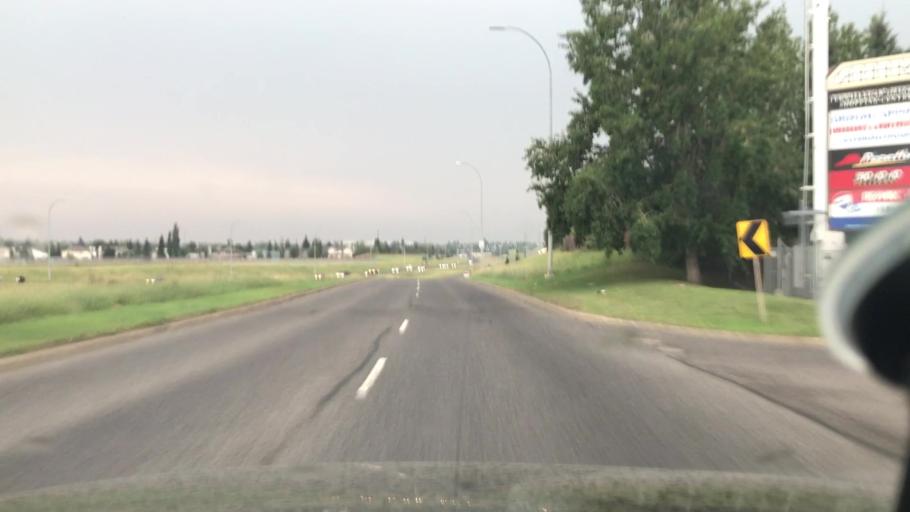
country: CA
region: Alberta
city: Edmonton
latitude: 53.4761
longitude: -113.5761
